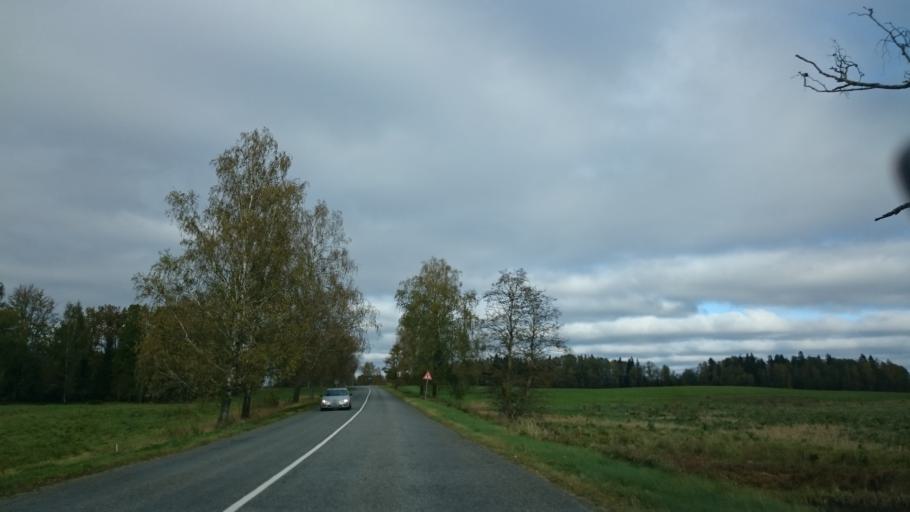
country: LV
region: Cesu Rajons
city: Cesis
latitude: 57.2805
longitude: 25.2653
